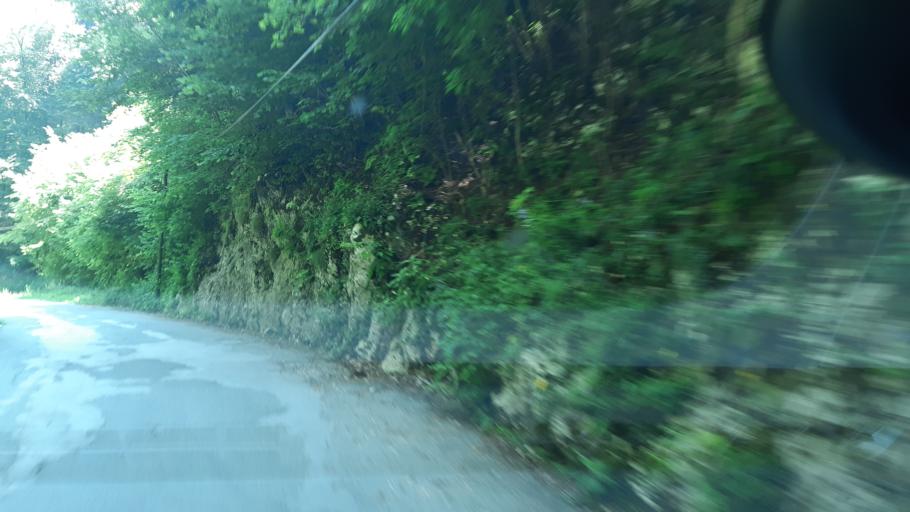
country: SI
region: Cerklje na Gorenjskem
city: Cerklje na Gorenjskem
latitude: 46.2817
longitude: 14.4949
